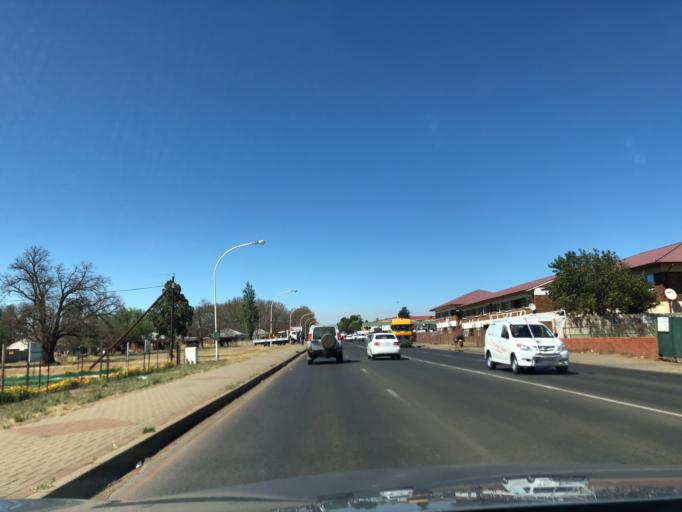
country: ZA
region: KwaZulu-Natal
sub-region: Amajuba District Municipality
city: Newcastle
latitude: -27.7545
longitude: 29.9403
